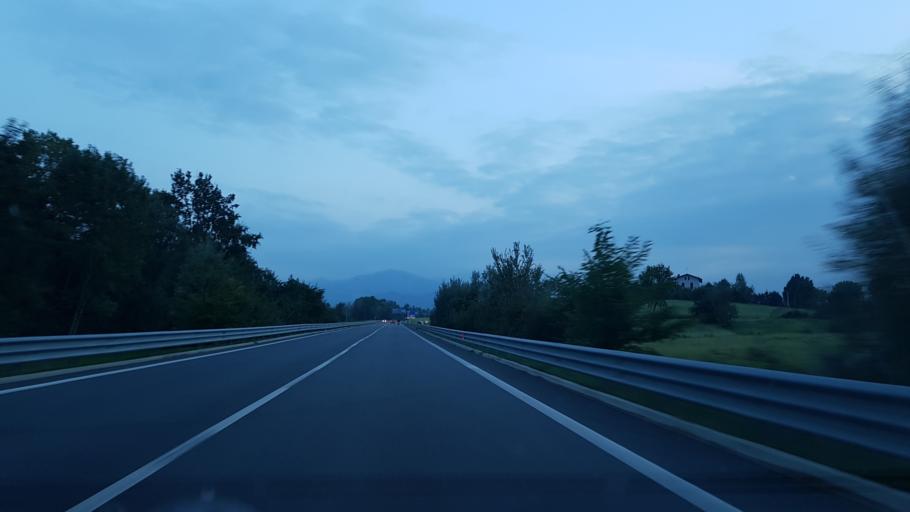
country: IT
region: Piedmont
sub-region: Provincia di Cuneo
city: Mondovi
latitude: 44.3974
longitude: 7.7969
